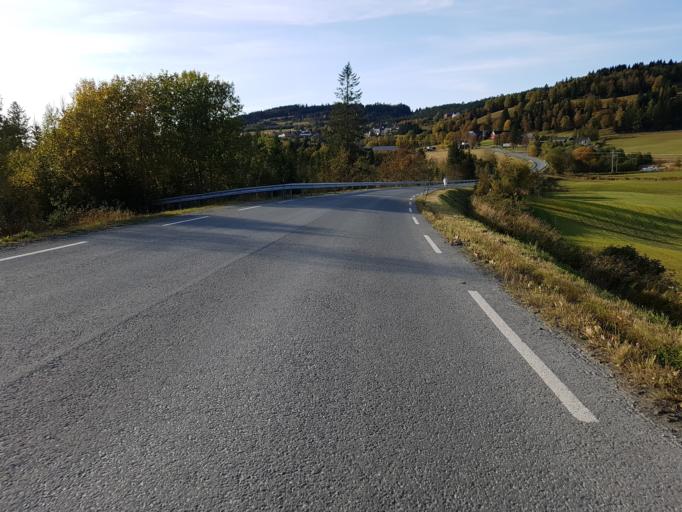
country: NO
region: Sor-Trondelag
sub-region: Klaebu
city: Klaebu
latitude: 63.3477
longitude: 10.5062
